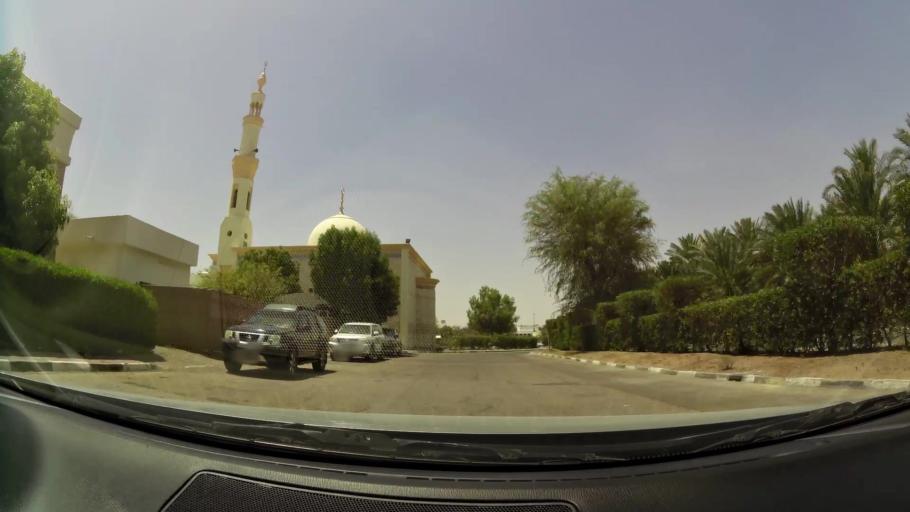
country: OM
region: Al Buraimi
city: Al Buraymi
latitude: 24.2735
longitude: 55.7554
